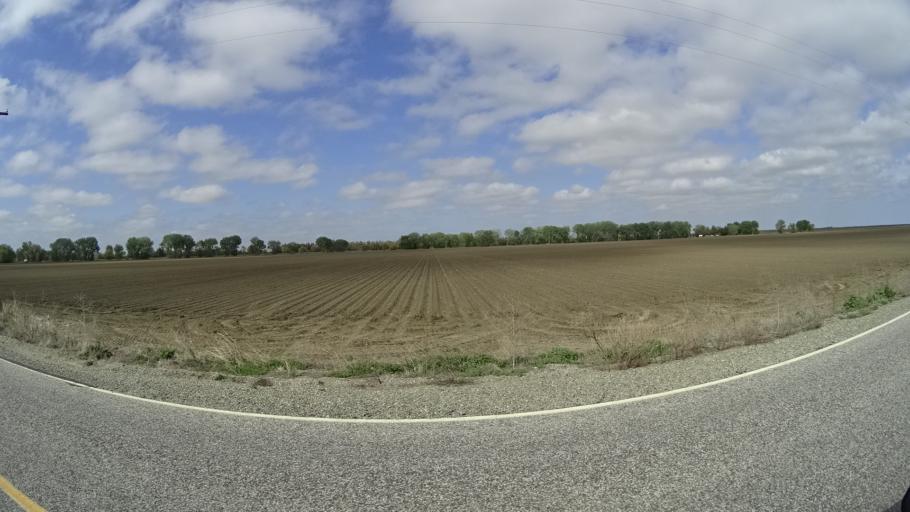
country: US
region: California
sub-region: Colusa County
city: Colusa
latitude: 39.4020
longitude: -121.9286
